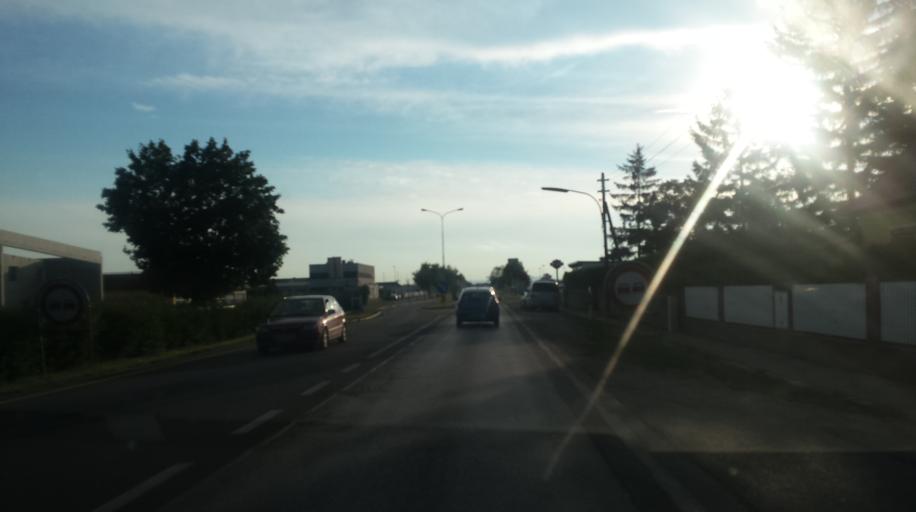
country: AT
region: Lower Austria
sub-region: Politischer Bezirk Ganserndorf
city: Parbasdorf
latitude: 48.3121
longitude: 16.6109
